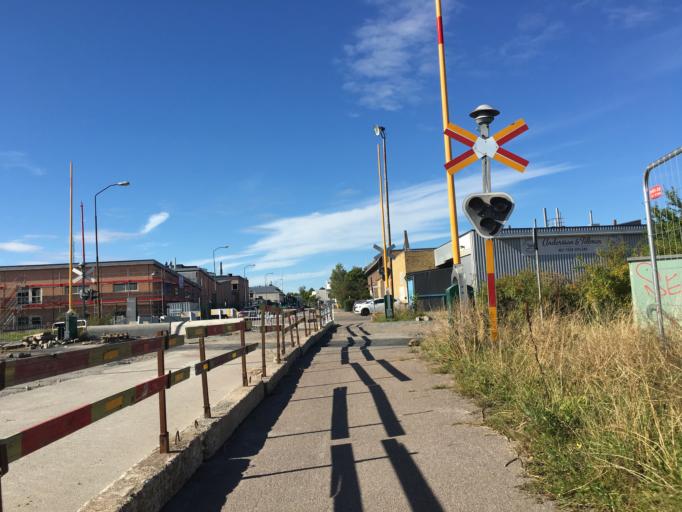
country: SE
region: Uppsala
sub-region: Uppsala Kommun
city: Uppsala
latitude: 59.8517
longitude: 17.6712
